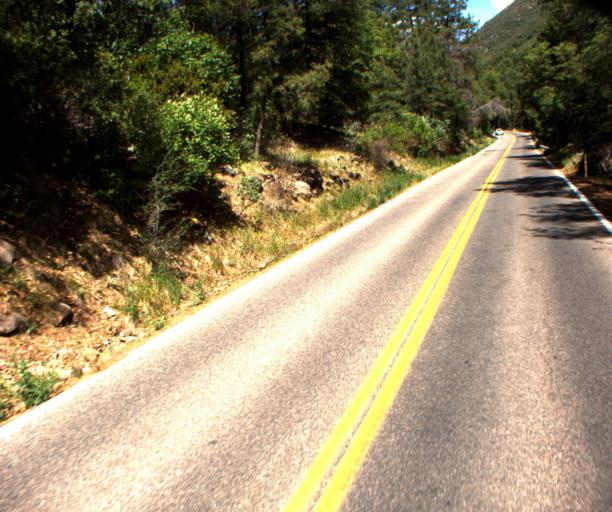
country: US
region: Arizona
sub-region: Coconino County
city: Sedona
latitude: 34.9326
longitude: -111.7417
